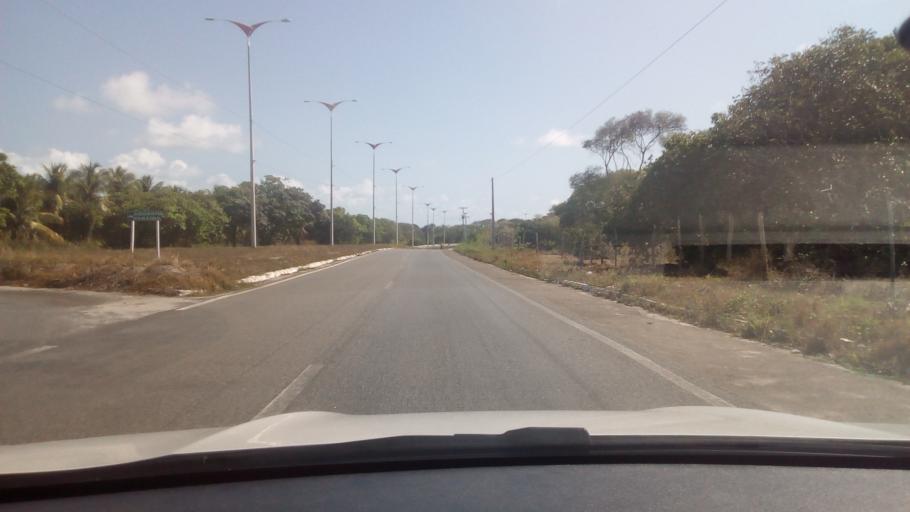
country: BR
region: Paraiba
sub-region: Joao Pessoa
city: Joao Pessoa
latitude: -7.1727
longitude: -34.8012
